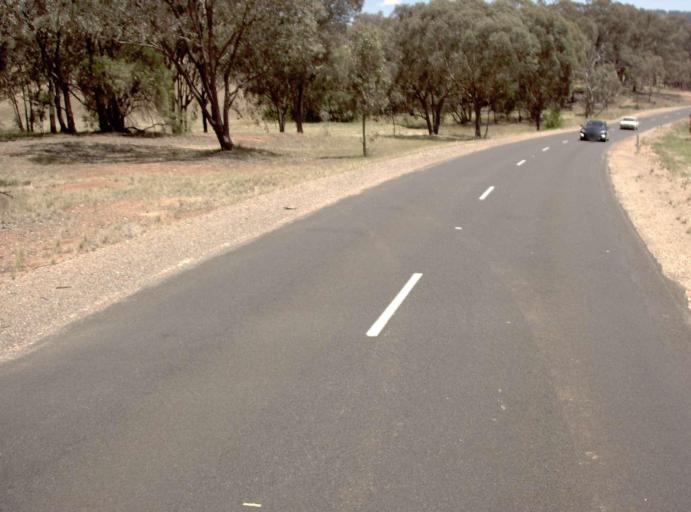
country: AU
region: Victoria
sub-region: East Gippsland
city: Bairnsdale
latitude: -37.1816
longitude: 147.7089
